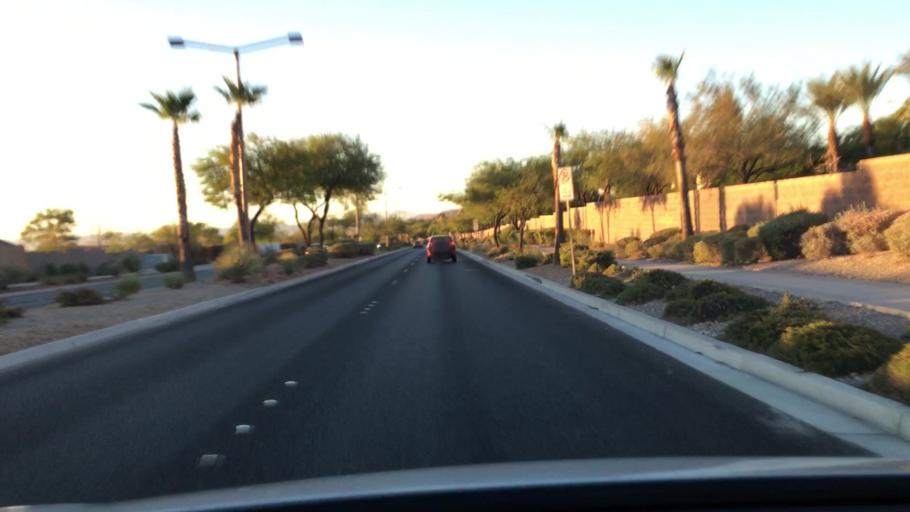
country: US
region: Nevada
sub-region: Clark County
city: Summerlin South
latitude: 36.1496
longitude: -115.3427
